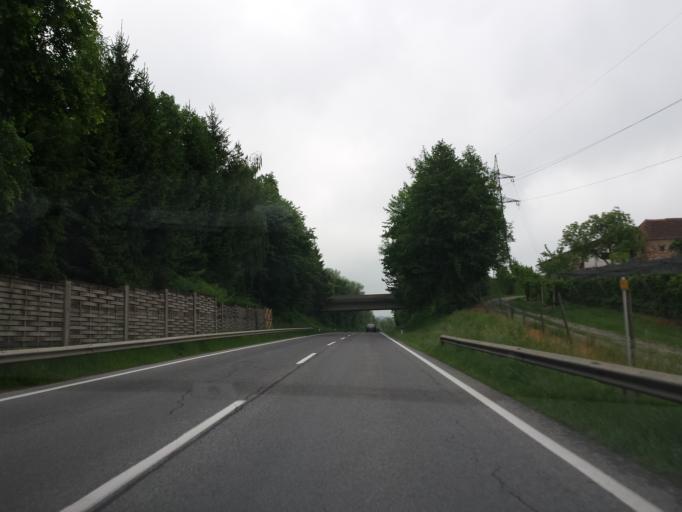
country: AT
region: Styria
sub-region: Politischer Bezirk Weiz
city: Krottendorf
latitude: 47.2120
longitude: 15.6469
